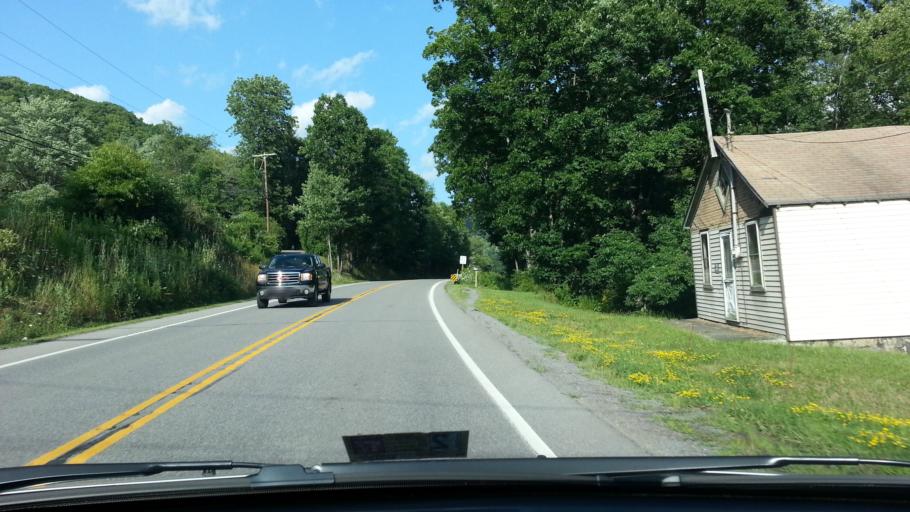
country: US
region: Pennsylvania
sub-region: Elk County
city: Saint Marys
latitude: 41.2521
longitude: -78.5149
